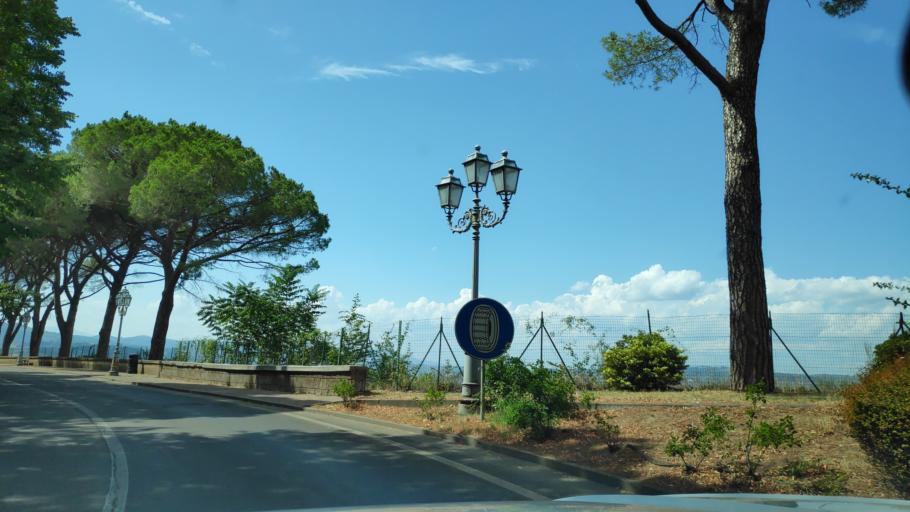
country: IT
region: Umbria
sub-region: Provincia di Terni
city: Orvieto
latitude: 42.7232
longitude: 12.1196
